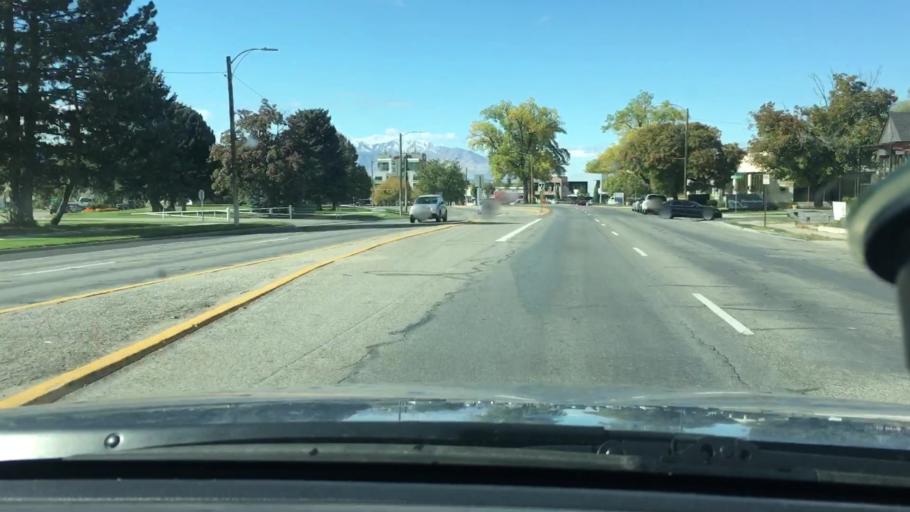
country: US
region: Utah
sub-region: Salt Lake County
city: Willard
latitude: 40.7259
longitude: -111.8502
